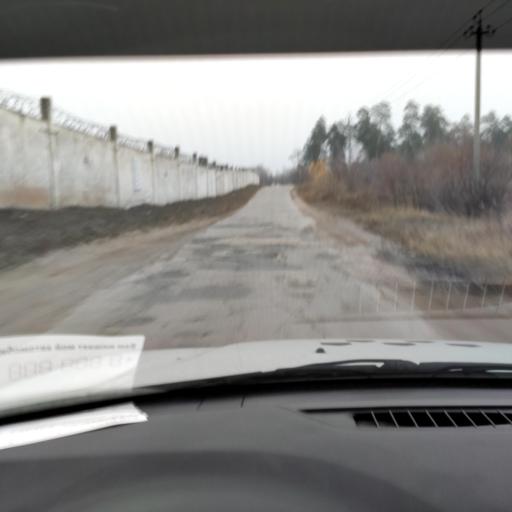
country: RU
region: Samara
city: Zhigulevsk
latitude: 53.4686
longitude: 49.5576
